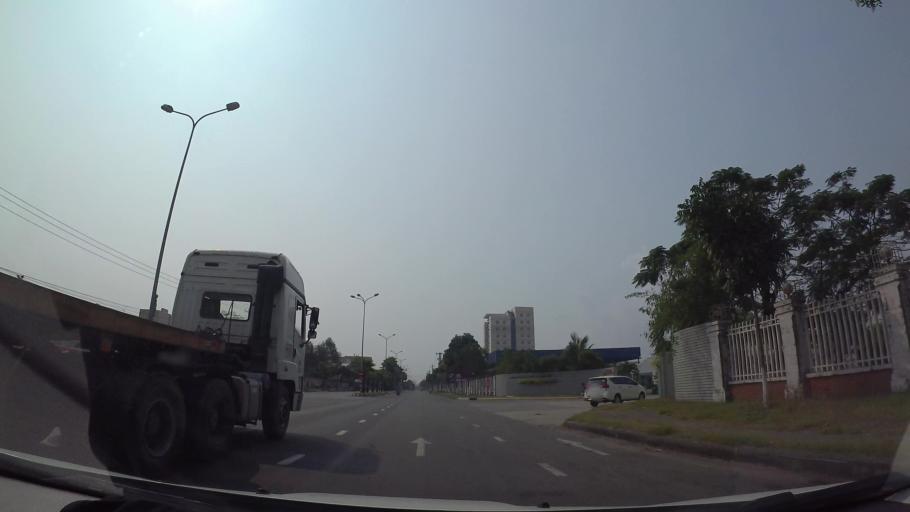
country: VN
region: Da Nang
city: Da Nang
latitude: 16.1099
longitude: 108.2453
